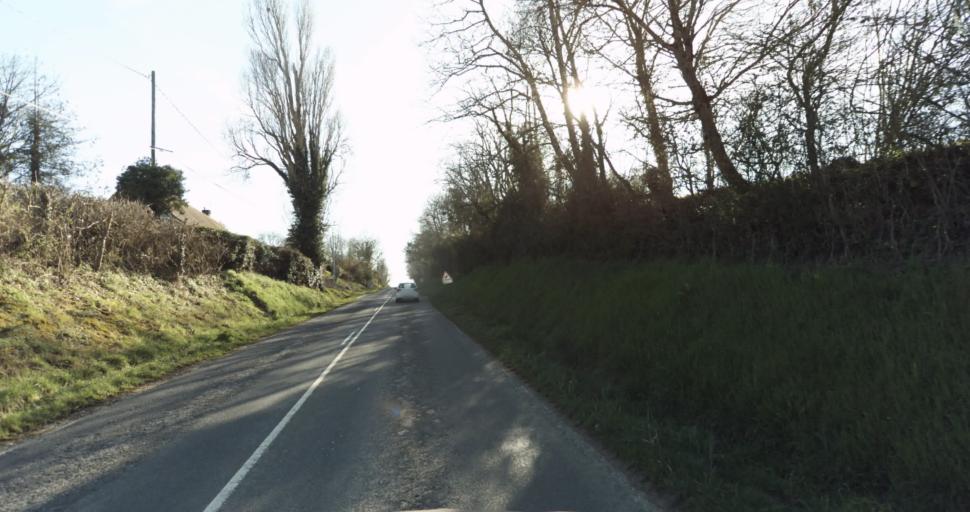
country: FR
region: Lower Normandy
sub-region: Departement du Calvados
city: Saint-Pierre-sur-Dives
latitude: 49.0311
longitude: -0.0007
